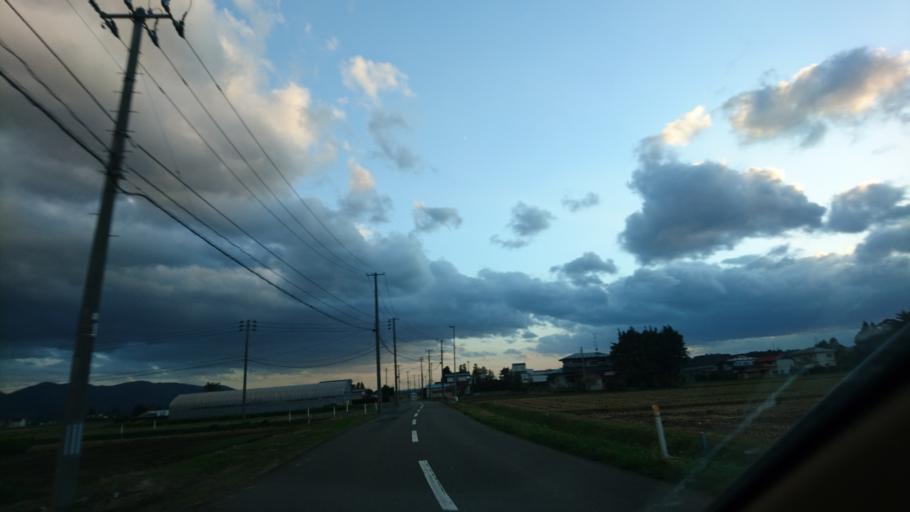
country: JP
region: Iwate
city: Mizusawa
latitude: 39.1025
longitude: 141.1475
